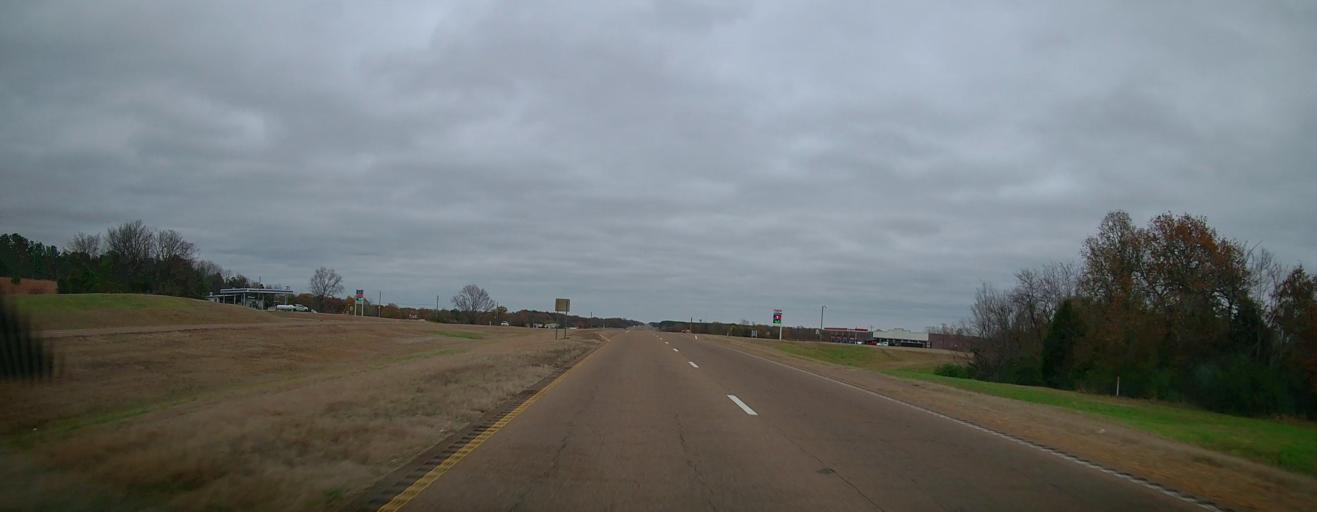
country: US
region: Mississippi
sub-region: Marshall County
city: Holly Springs
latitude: 34.9461
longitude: -89.3901
